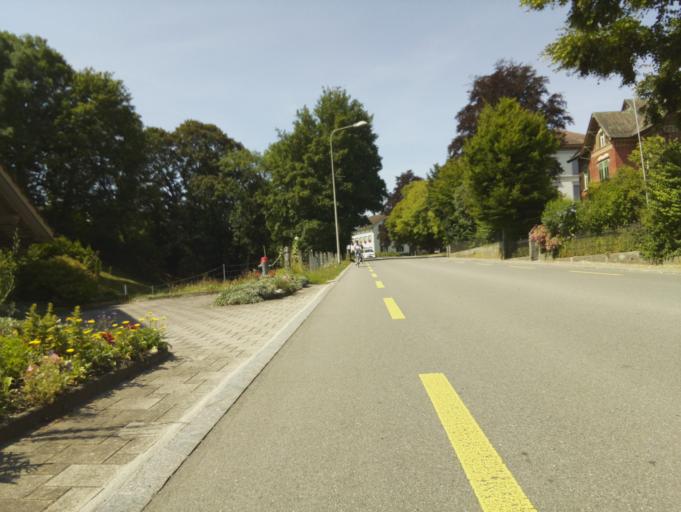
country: CH
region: Zurich
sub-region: Bezirk Andelfingen
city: Grossandelfingen
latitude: 47.5964
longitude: 8.6784
